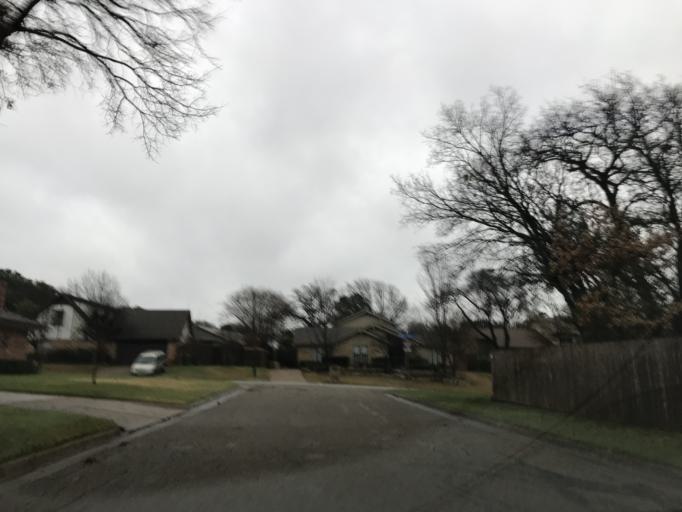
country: US
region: Texas
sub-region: Tarrant County
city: Arlington
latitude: 32.7735
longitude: -97.1086
